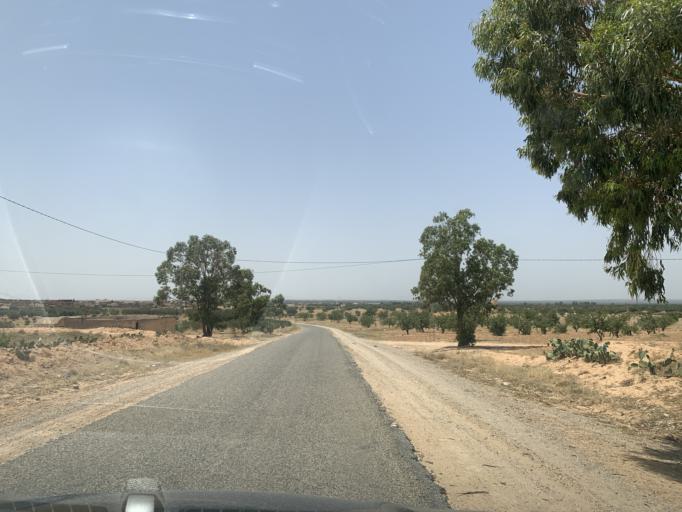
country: TN
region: Al Mahdiyah
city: Shurban
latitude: 35.1622
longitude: 10.2464
